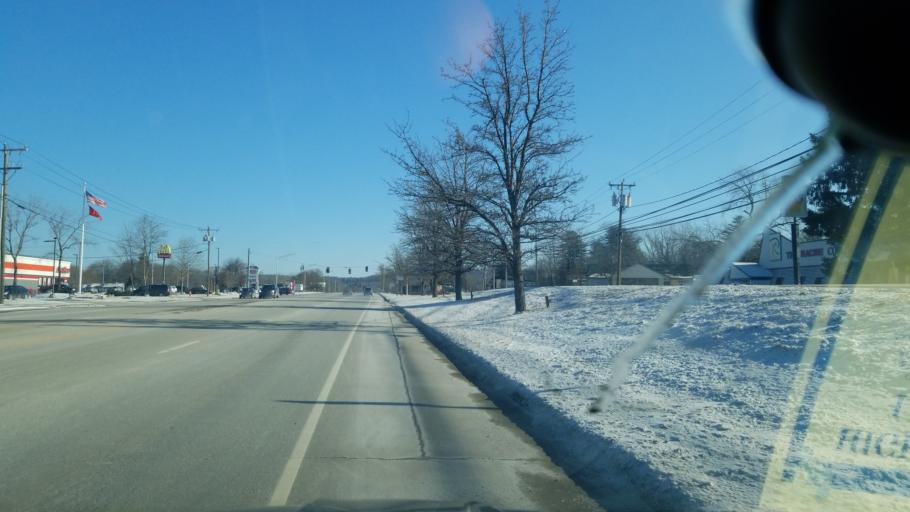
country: US
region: Connecticut
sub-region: Windham County
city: East Brooklyn
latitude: 41.7986
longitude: -71.9034
